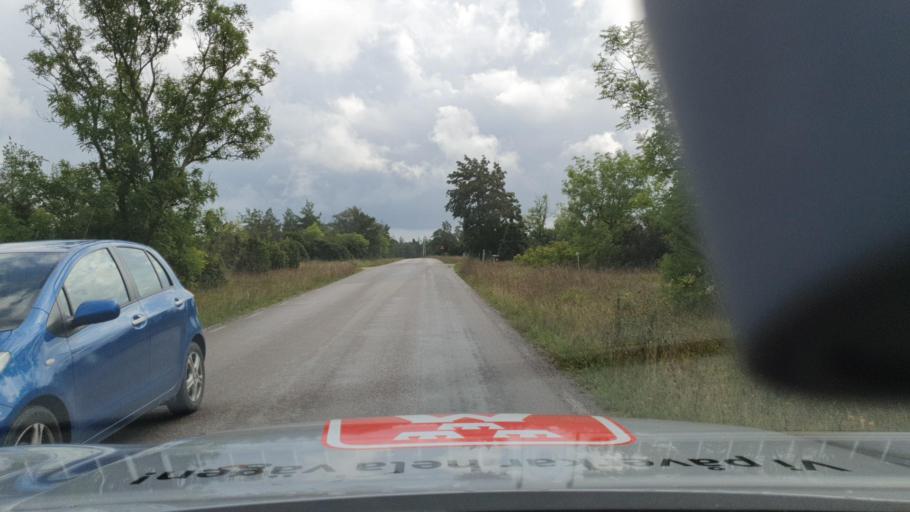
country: SE
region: Gotland
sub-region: Gotland
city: Slite
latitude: 57.7204
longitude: 18.7512
